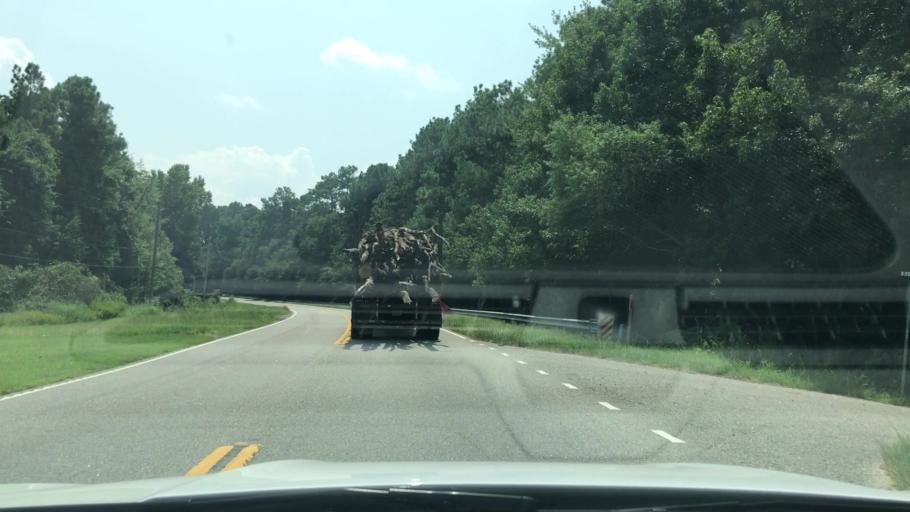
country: US
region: South Carolina
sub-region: Georgetown County
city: Georgetown
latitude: 33.4767
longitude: -79.2777
